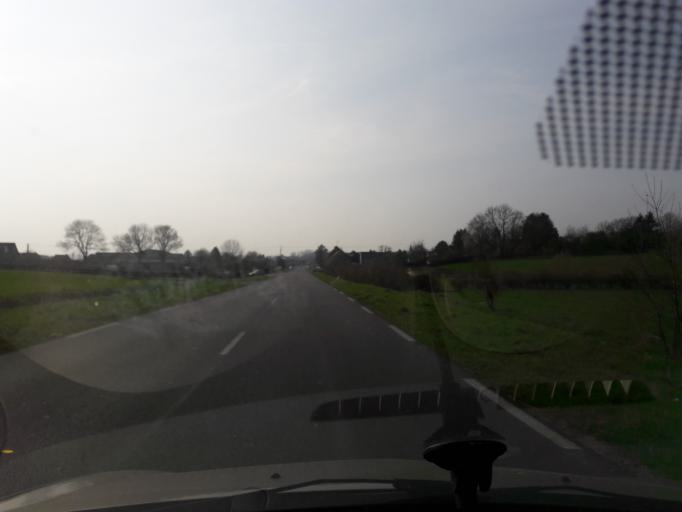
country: FR
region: Nord-Pas-de-Calais
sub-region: Departement du Nord
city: Recquignies
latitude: 50.2586
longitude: 4.0367
